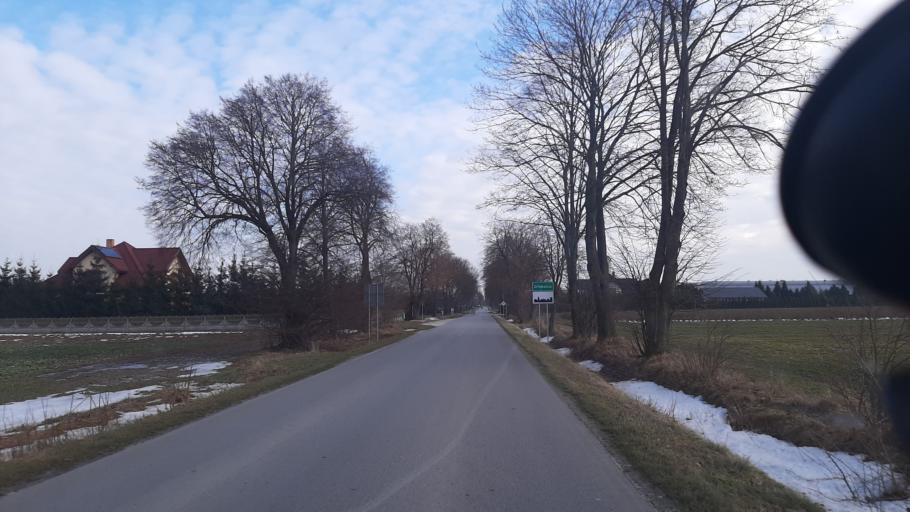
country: PL
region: Lublin Voivodeship
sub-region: Powiat lubartowski
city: Uscimow Stary
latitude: 51.4807
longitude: 22.9069
